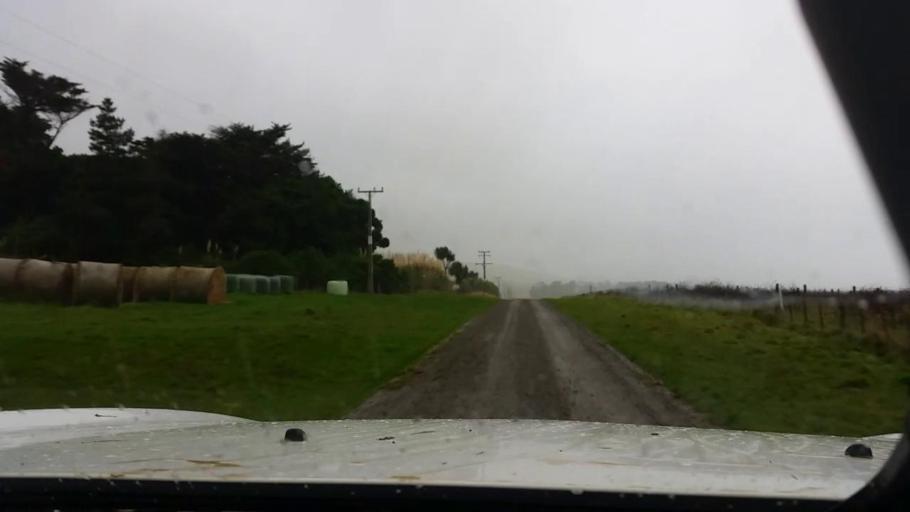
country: NZ
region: Wellington
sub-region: Masterton District
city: Masterton
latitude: -41.2579
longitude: 175.9025
